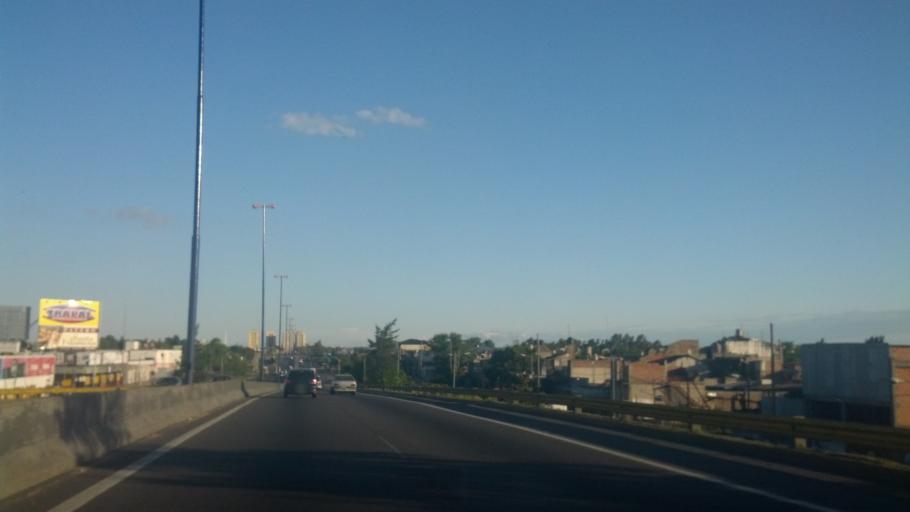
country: AR
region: Buenos Aires
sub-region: Partido de Lomas de Zamora
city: Lomas de Zamora
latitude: -34.7264
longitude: -58.4422
